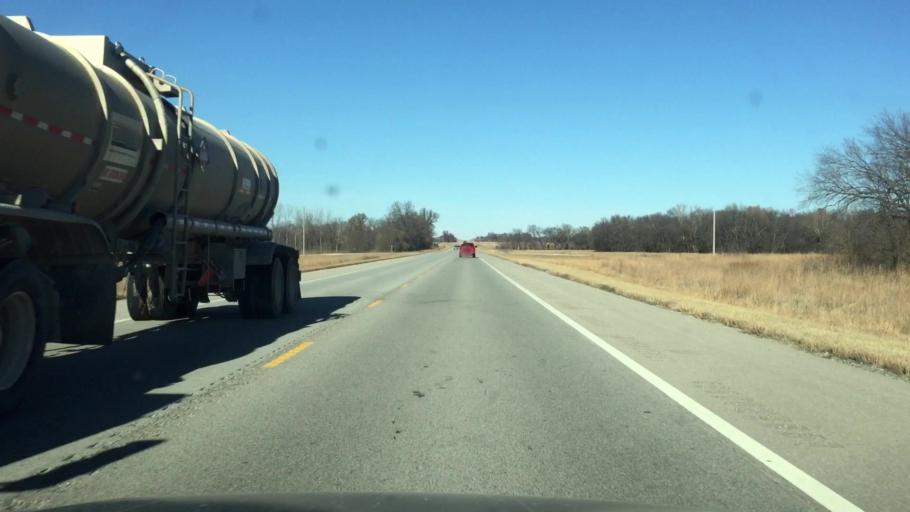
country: US
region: Kansas
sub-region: Allen County
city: Iola
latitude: 37.9785
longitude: -95.3810
